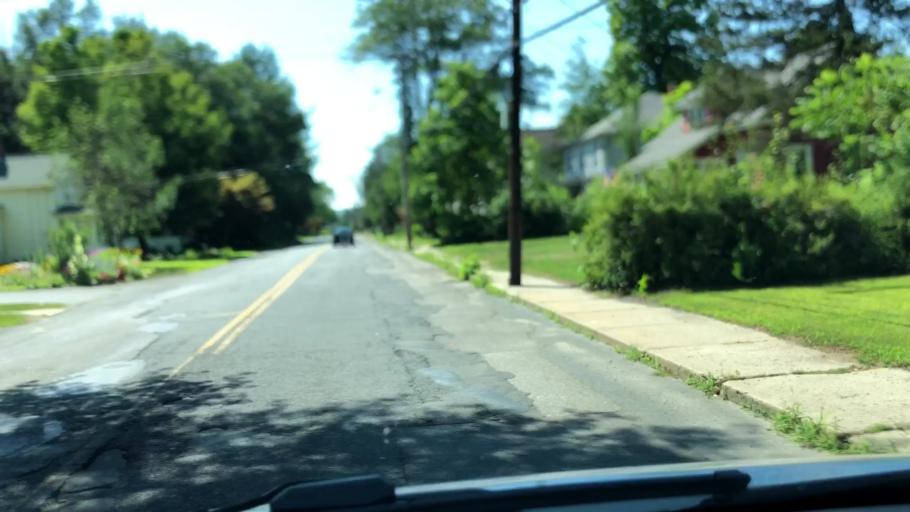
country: US
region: Massachusetts
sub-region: Hampshire County
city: Easthampton
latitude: 42.2754
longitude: -72.6474
